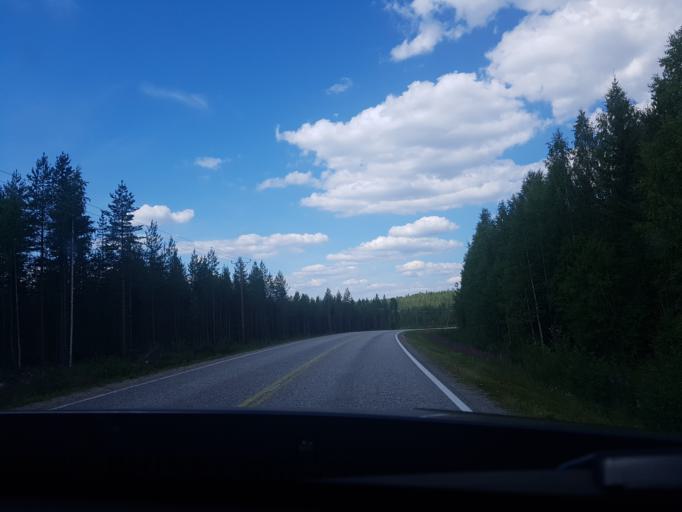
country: FI
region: Kainuu
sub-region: Kehys-Kainuu
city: Kuhmo
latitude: 64.2449
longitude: 29.8076
